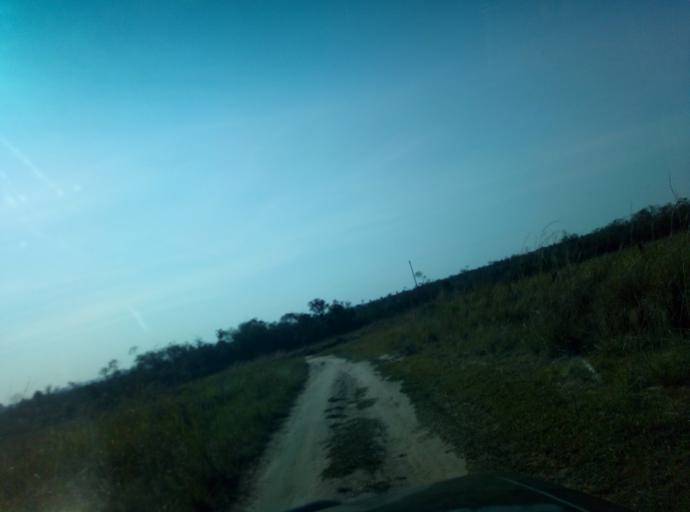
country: PY
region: Caaguazu
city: Doctor Cecilio Baez
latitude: -25.1910
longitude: -56.1925
